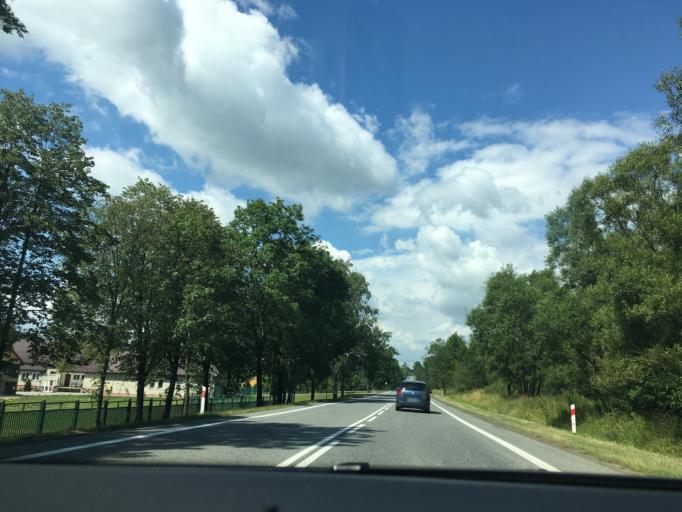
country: PL
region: Subcarpathian Voivodeship
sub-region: Powiat krosnienski
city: Dukla
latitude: 49.5751
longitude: 21.7017
